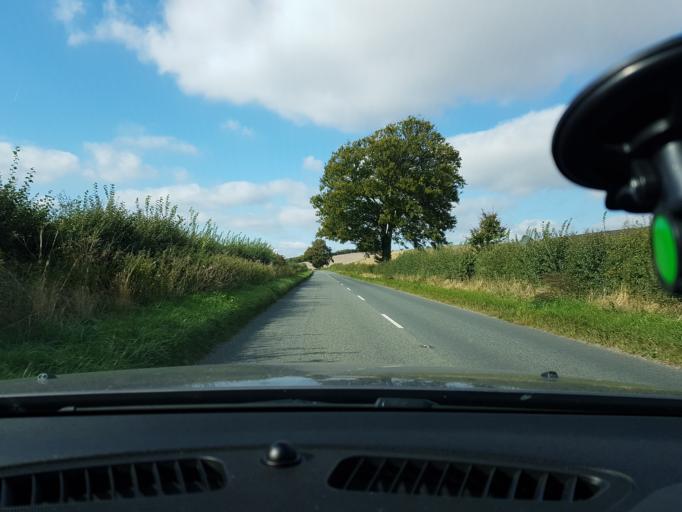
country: GB
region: England
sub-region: Wiltshire
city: Aldbourne
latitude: 51.4852
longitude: -1.6352
